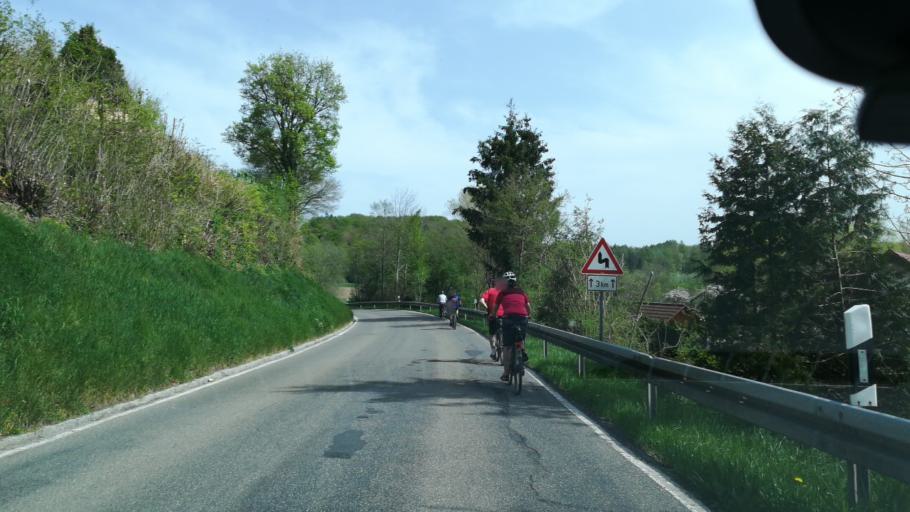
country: DE
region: Baden-Wuerttemberg
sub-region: Freiburg Region
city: Allensbach
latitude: 47.7336
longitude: 9.1194
